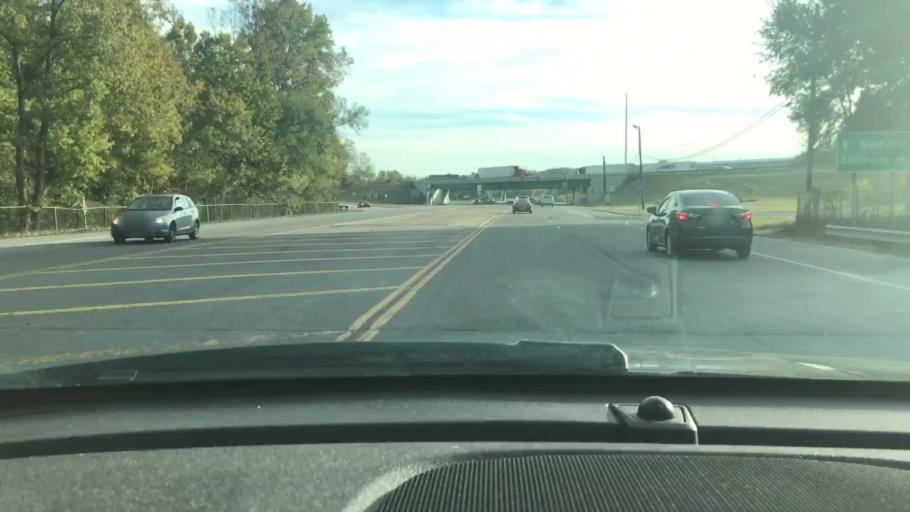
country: US
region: Tennessee
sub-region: Sumner County
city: Millersville
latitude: 36.3494
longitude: -86.7159
